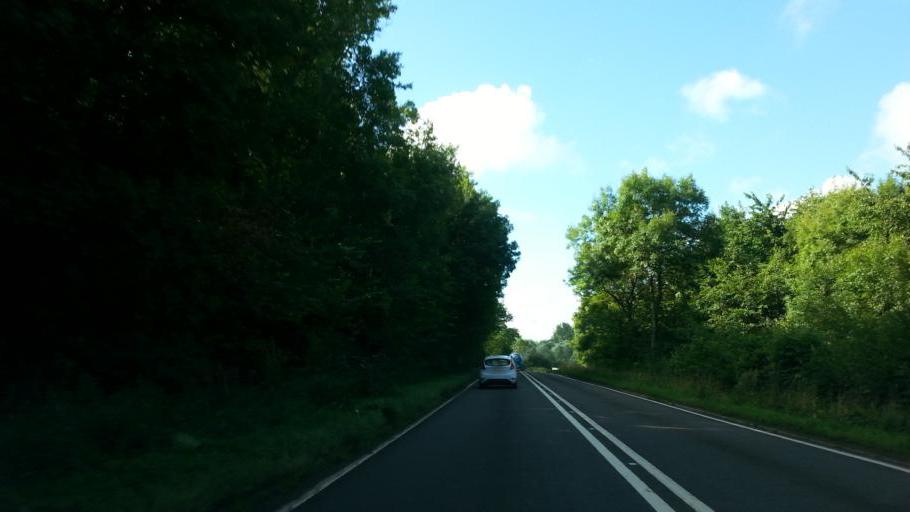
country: GB
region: England
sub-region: District of Rutland
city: Morcott
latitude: 52.5219
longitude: -0.5921
